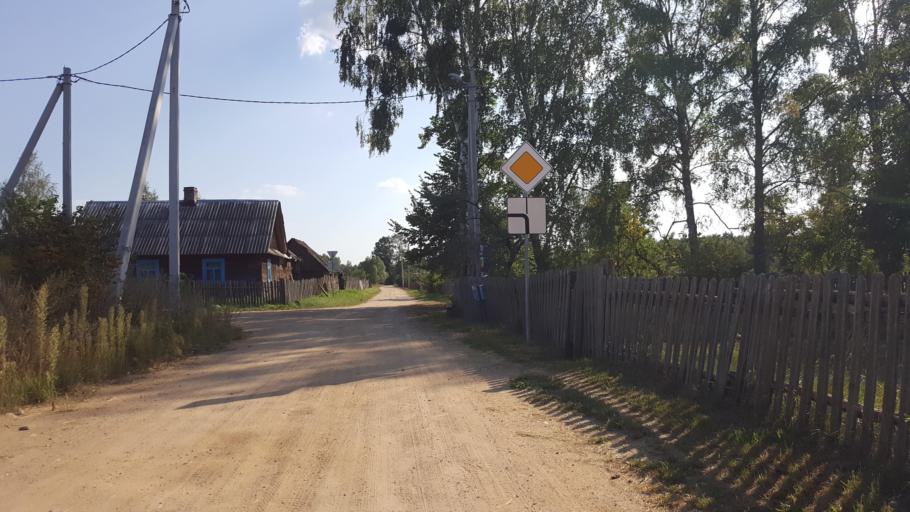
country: BY
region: Brest
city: Kamyanyuki
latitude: 52.5624
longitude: 23.6320
